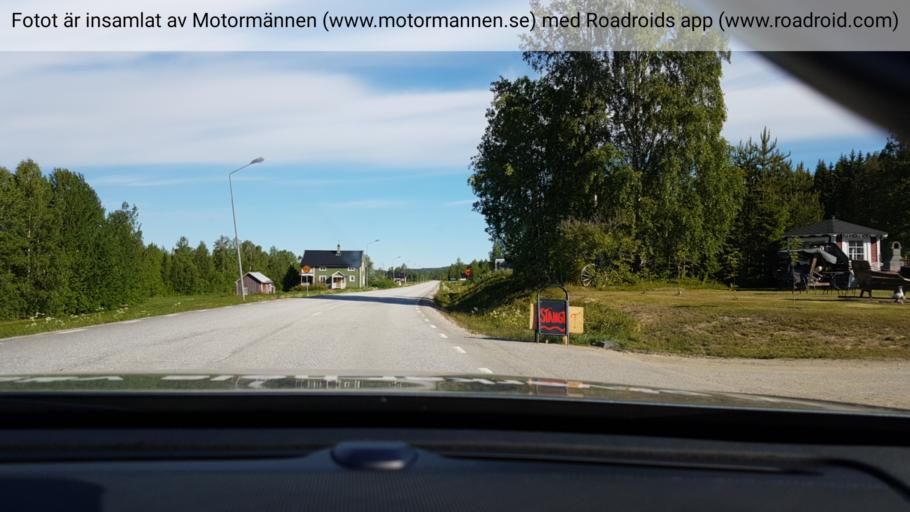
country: SE
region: Vaesterbotten
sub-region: Vindelns Kommun
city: Vindeln
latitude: 64.1395
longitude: 19.5215
